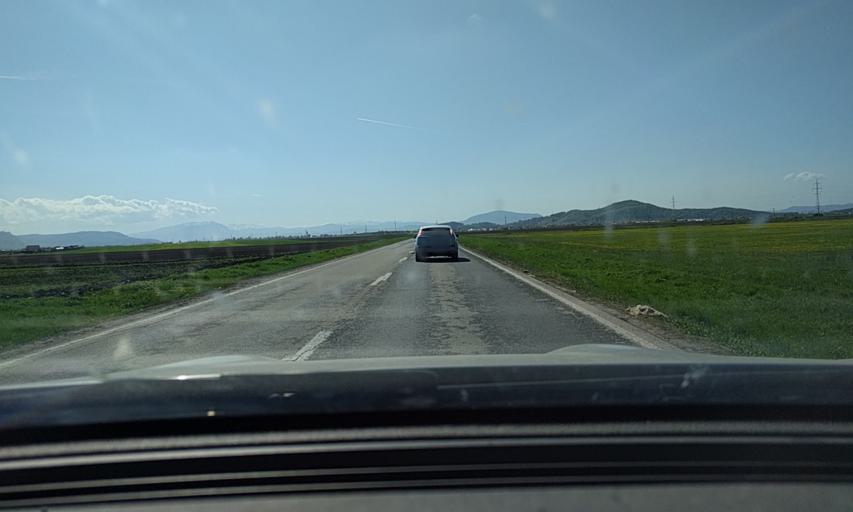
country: RO
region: Brasov
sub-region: Comuna Prejmer
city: Prejmer
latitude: 45.7140
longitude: 25.7298
